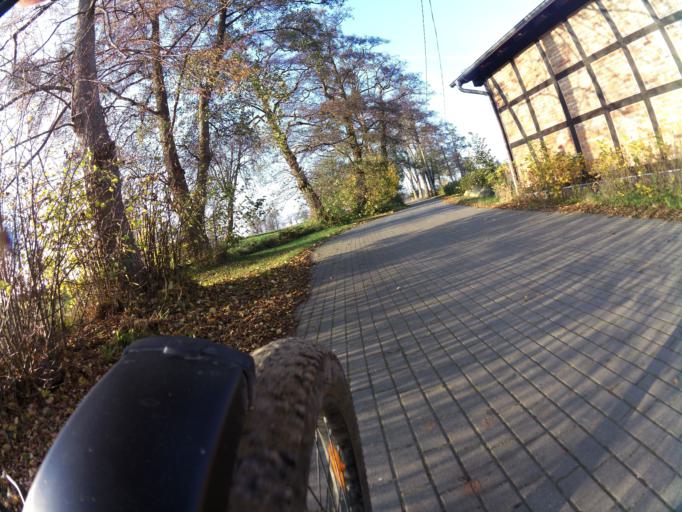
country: PL
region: Pomeranian Voivodeship
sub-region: Powiat pucki
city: Krokowa
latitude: 54.7503
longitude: 18.1895
